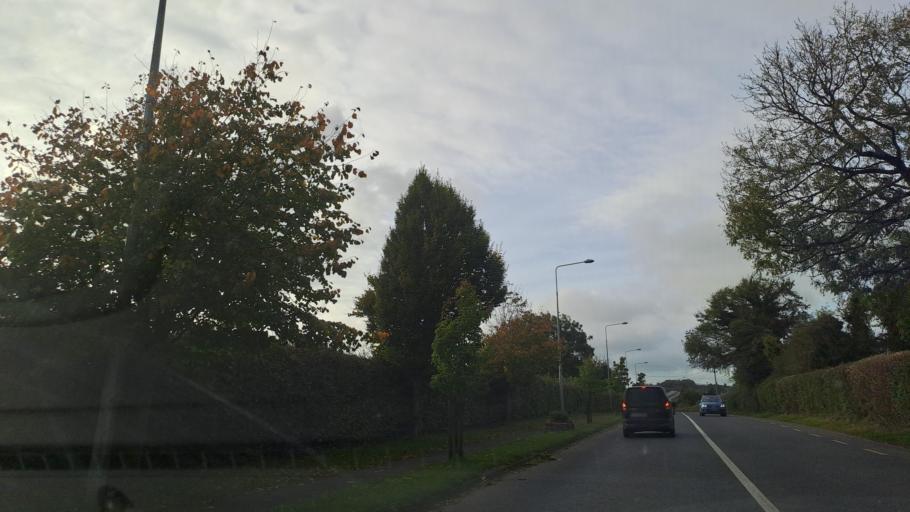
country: IE
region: Ulster
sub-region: An Cabhan
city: Kingscourt
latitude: 53.8195
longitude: -6.7433
